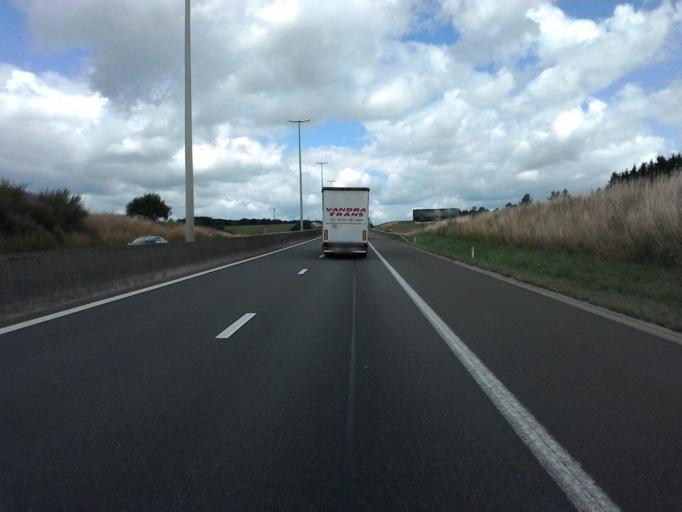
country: BE
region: Wallonia
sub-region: Province du Luxembourg
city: Leglise
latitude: 49.7997
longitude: 5.5222
